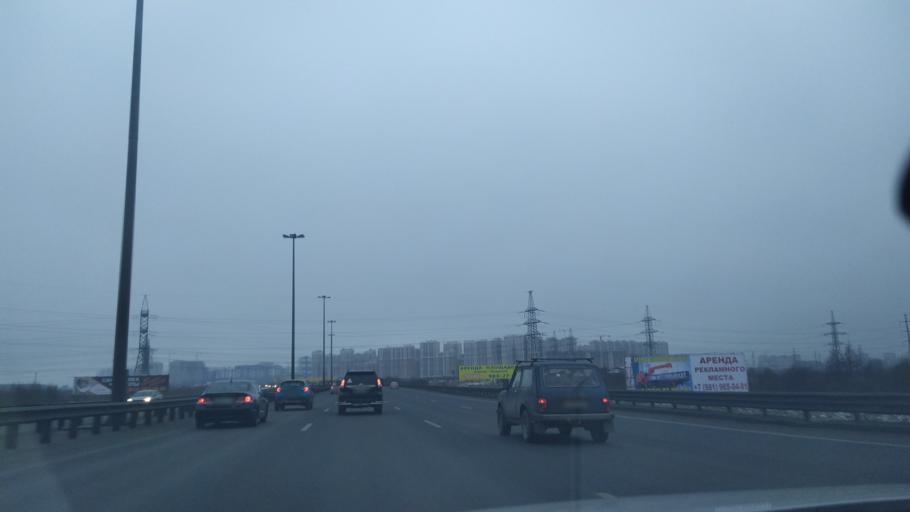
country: RU
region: St.-Petersburg
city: Krasnogvargeisky
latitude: 59.9271
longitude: 30.5326
